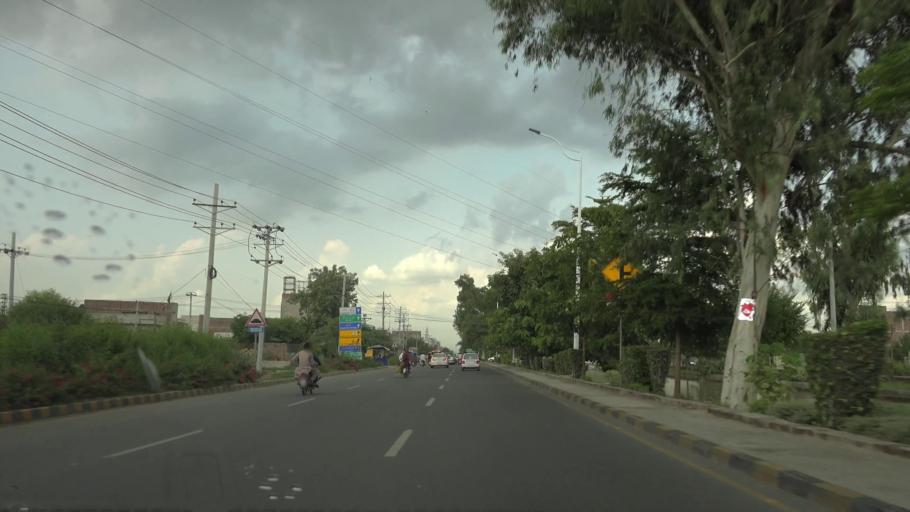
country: PK
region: Punjab
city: Faisalabad
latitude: 31.4321
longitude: 73.1225
